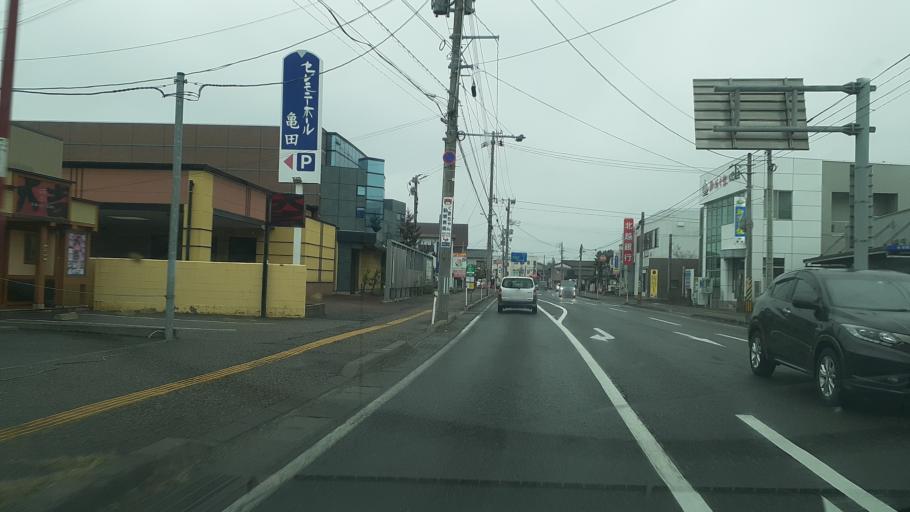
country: JP
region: Niigata
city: Kameda-honcho
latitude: 37.8761
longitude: 139.1061
